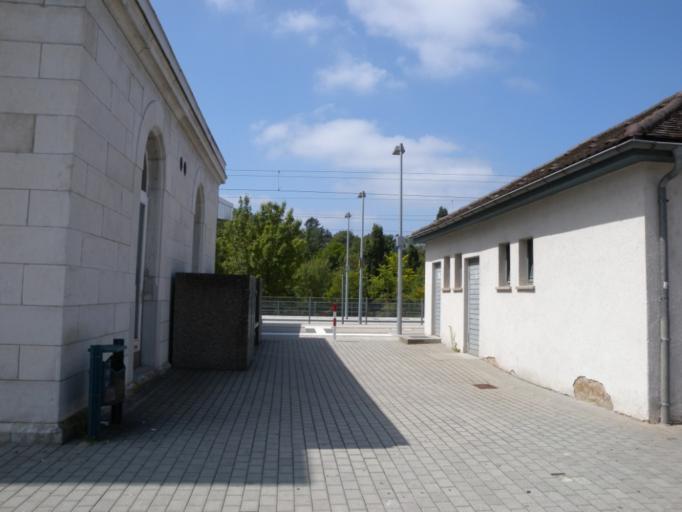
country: DE
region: Baden-Wuerttemberg
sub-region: Regierungsbezirk Stuttgart
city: Ellwangen
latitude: 48.9643
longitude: 10.1300
